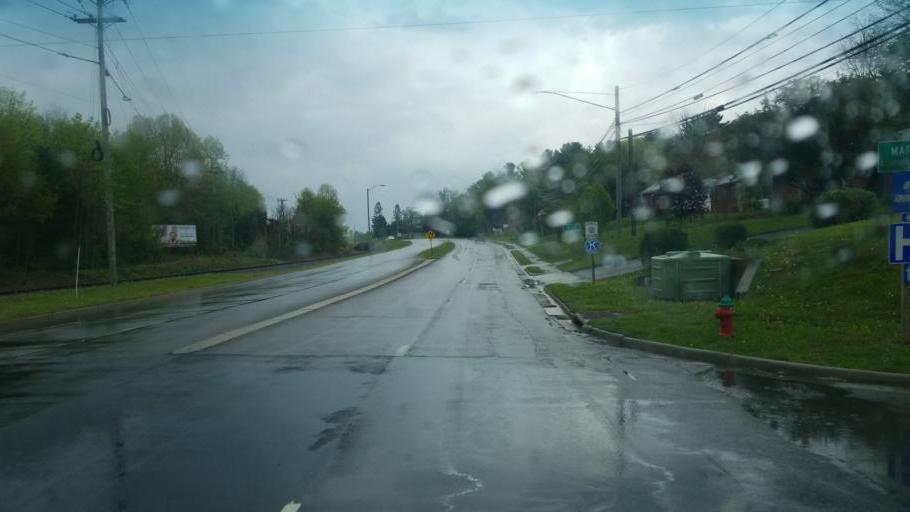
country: US
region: Virginia
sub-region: Smyth County
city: Marion
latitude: 36.8243
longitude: -81.5373
